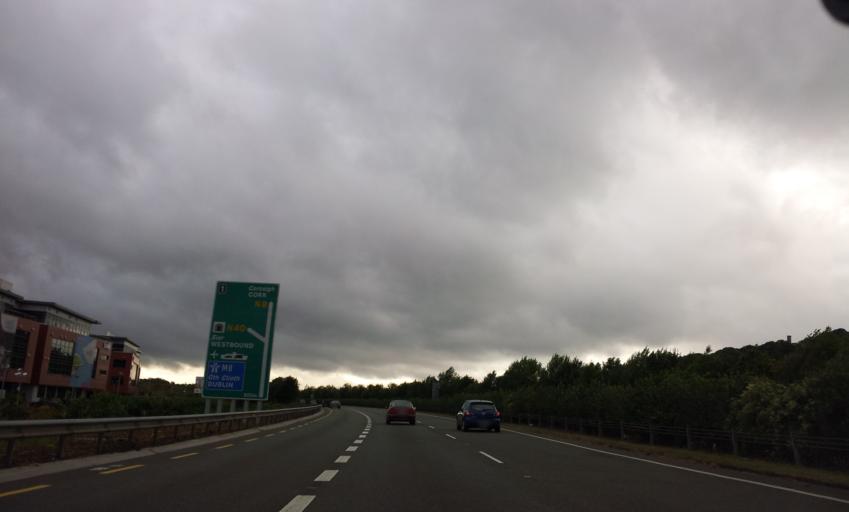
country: IE
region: Munster
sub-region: County Cork
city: Passage West
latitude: 51.9066
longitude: -8.3627
